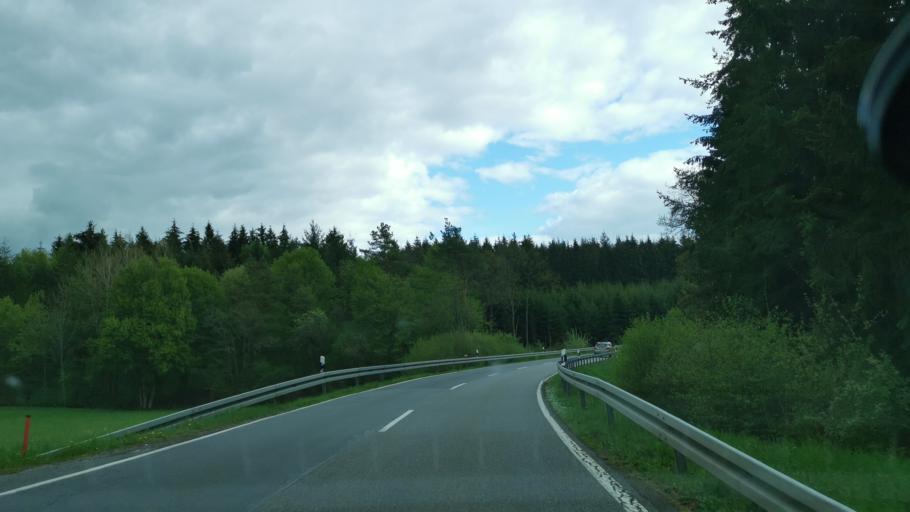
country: DE
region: Baden-Wuerttemberg
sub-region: Karlsruhe Region
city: Osterburken
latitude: 49.4627
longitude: 9.4179
